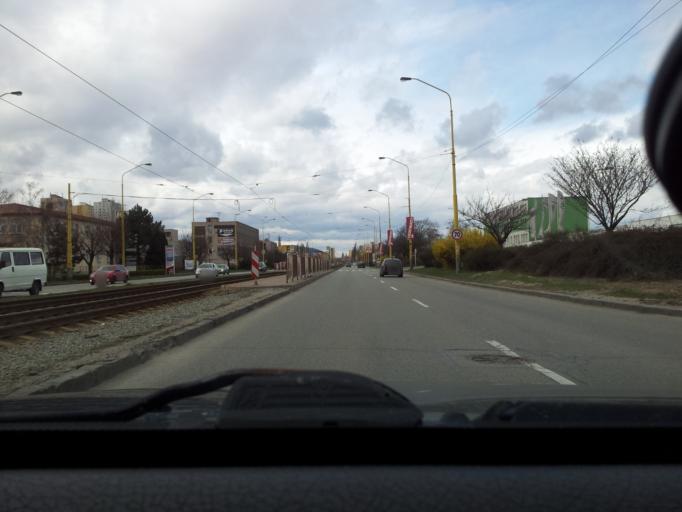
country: SK
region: Kosicky
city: Kosice
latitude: 48.6980
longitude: 21.2640
